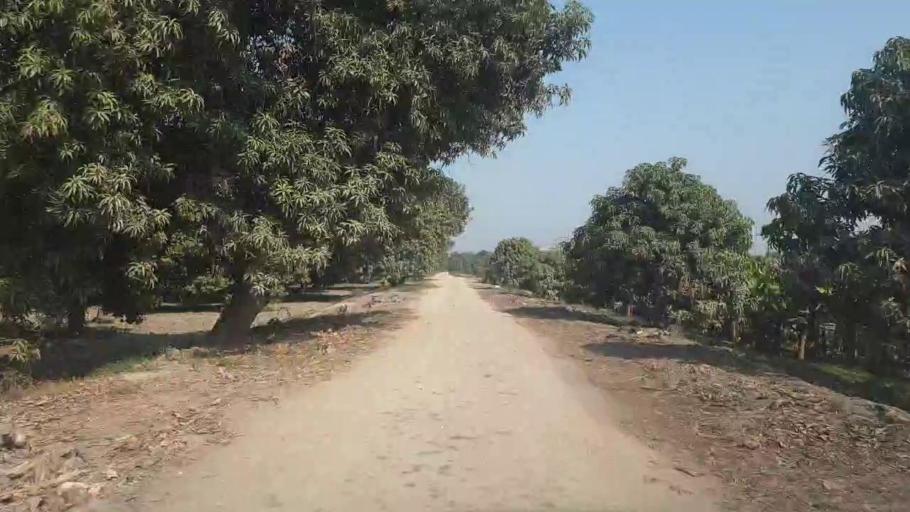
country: PK
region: Sindh
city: Tando Allahyar
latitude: 25.4679
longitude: 68.7820
